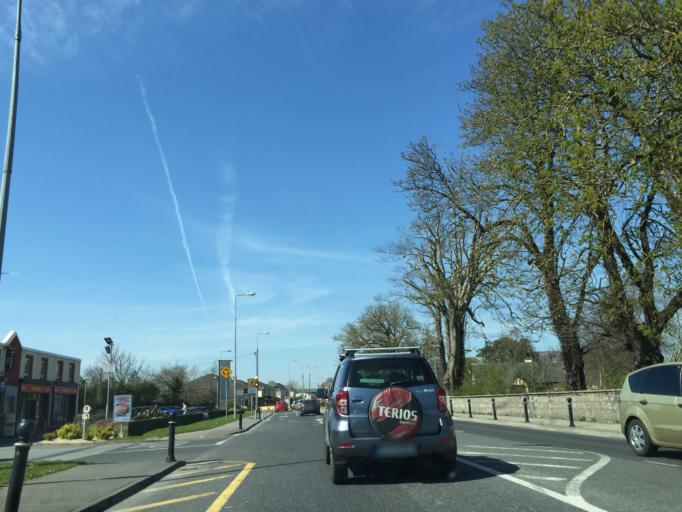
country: IE
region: Munster
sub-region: Ciarrai
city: Tralee
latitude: 52.2651
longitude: -9.6783
